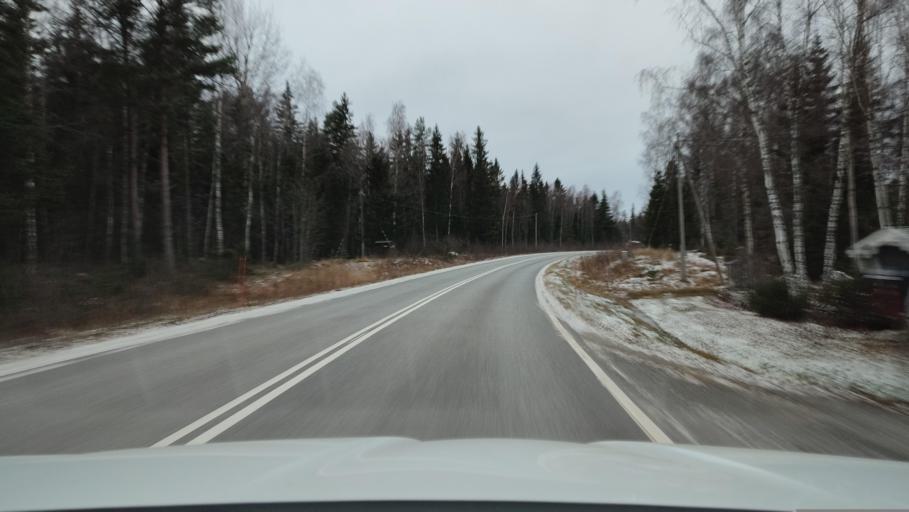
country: FI
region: Ostrobothnia
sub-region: Vaasa
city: Replot
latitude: 63.2663
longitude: 21.3498
